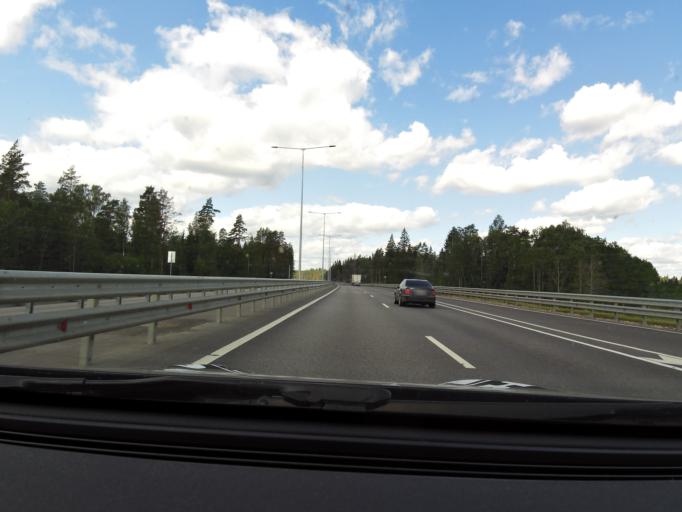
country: RU
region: Tverskaya
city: Vydropuzhsk
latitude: 57.2714
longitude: 34.8585
